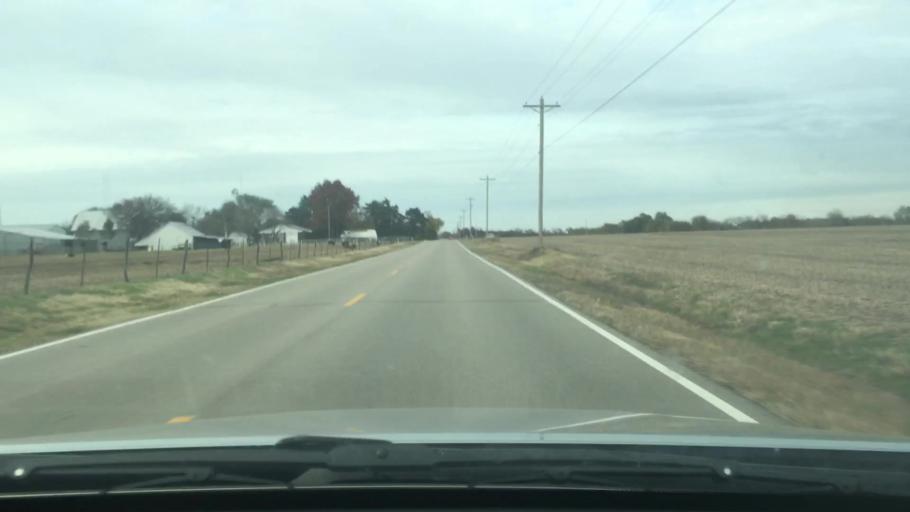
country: US
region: Kansas
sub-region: Sedgwick County
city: Maize
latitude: 37.7407
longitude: -97.4992
